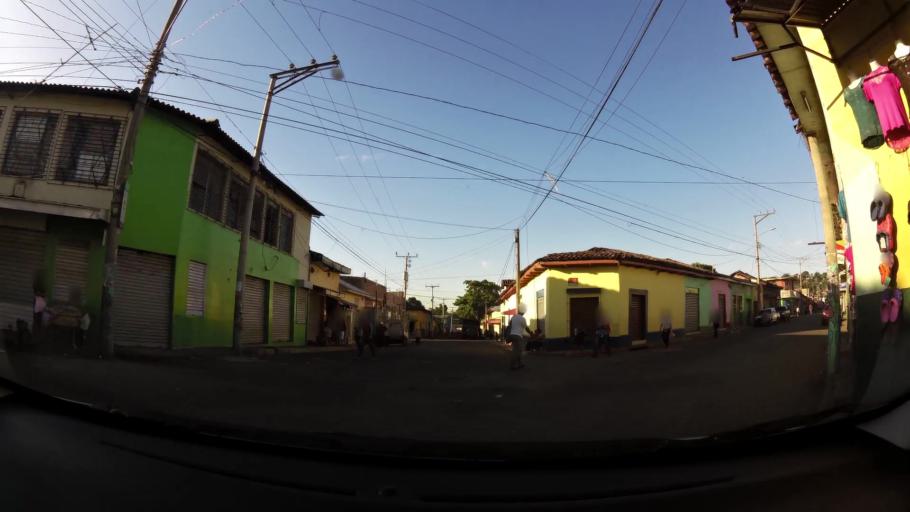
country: SV
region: Sonsonate
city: Sonsonate
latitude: 13.7218
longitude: -89.7306
